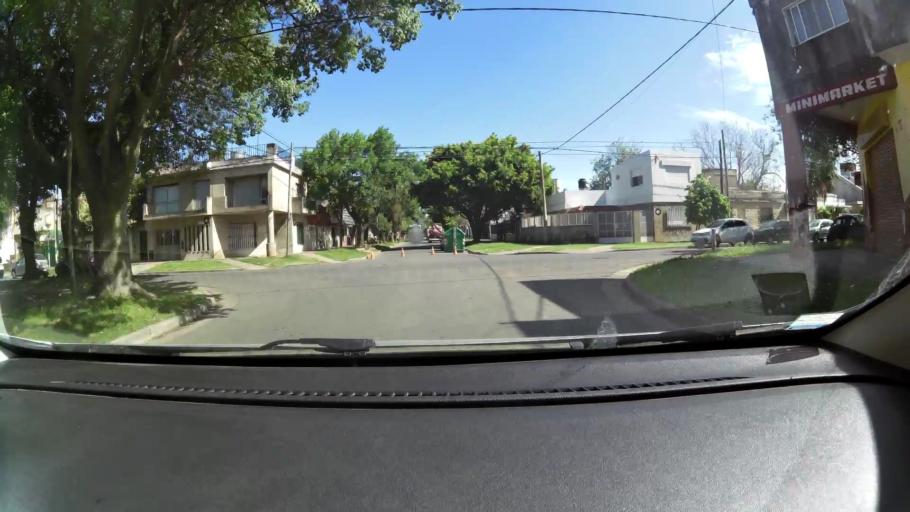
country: AR
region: Santa Fe
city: Granadero Baigorria
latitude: -32.9346
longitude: -60.7187
